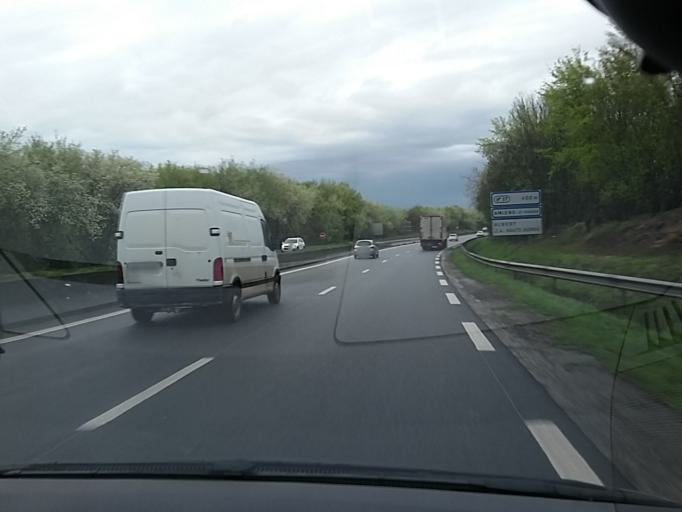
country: FR
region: Picardie
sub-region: Departement de la Somme
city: Camon
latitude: 49.9066
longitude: 2.3472
